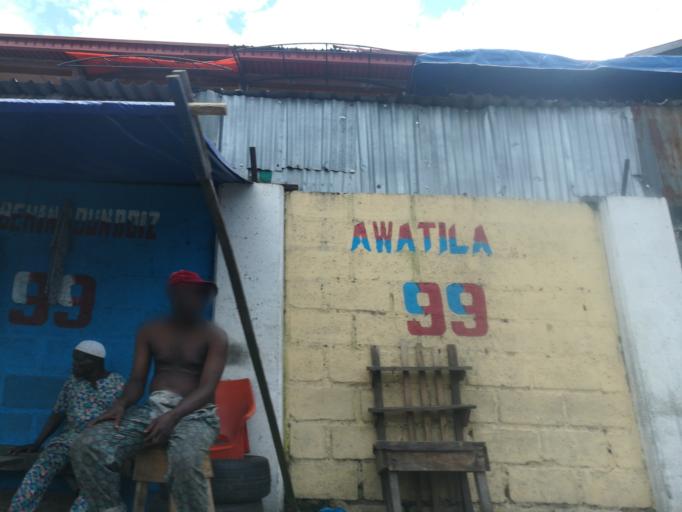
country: NG
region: Lagos
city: Lagos
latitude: 6.4633
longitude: 3.3846
